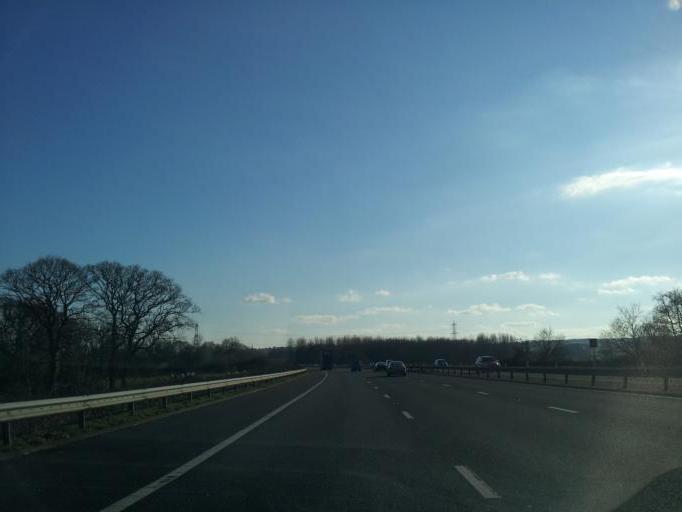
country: GB
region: England
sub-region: Devon
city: Heavitree
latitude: 50.7757
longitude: -3.4571
